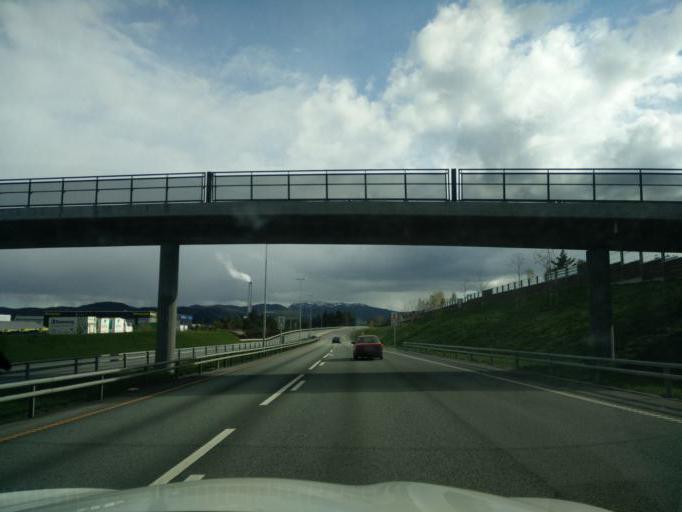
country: NO
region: Sor-Trondelag
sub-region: Trondheim
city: Trondheim
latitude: 63.3567
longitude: 10.3710
